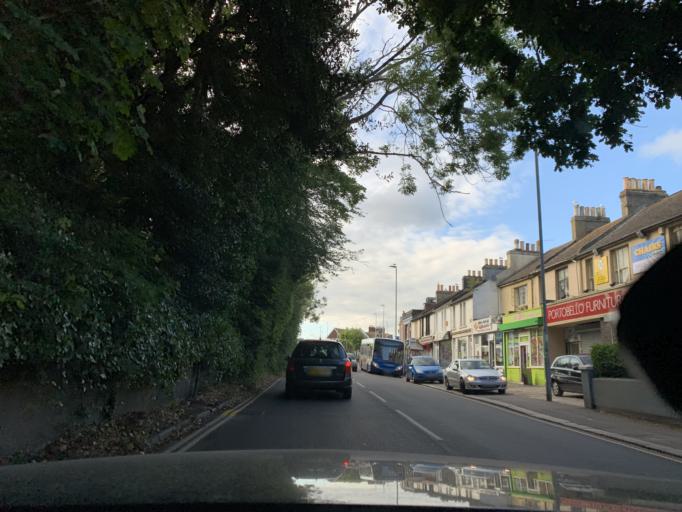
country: GB
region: England
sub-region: East Sussex
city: Saint Leonards-on-Sea
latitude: 50.8664
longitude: 0.5561
